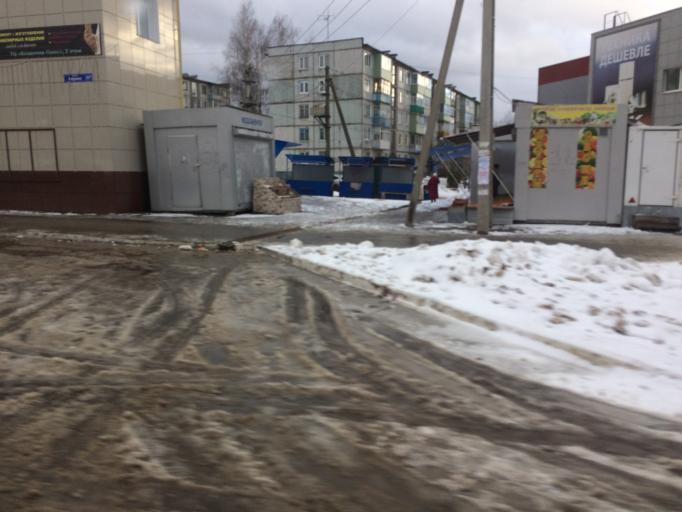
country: RU
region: Tula
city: Suvorov
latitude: 54.1199
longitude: 36.5031
